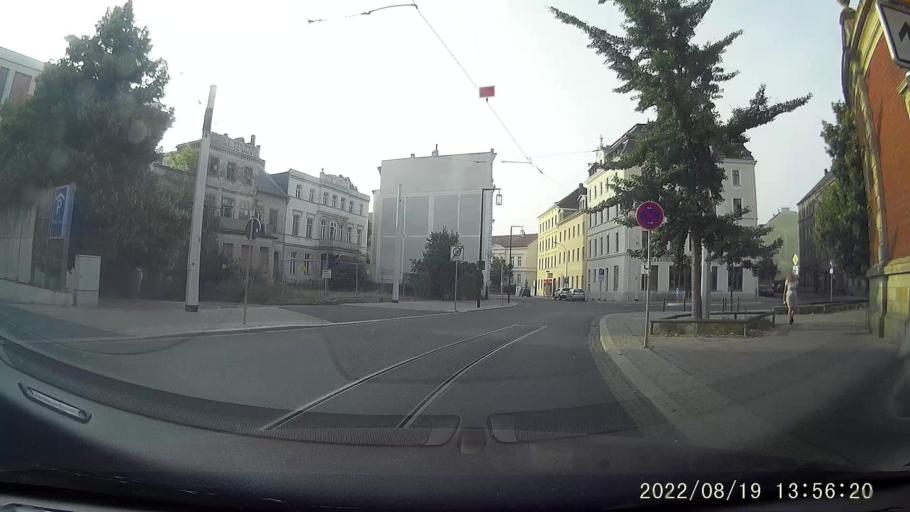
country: DE
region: Saxony
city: Goerlitz
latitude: 51.1545
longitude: 14.9646
